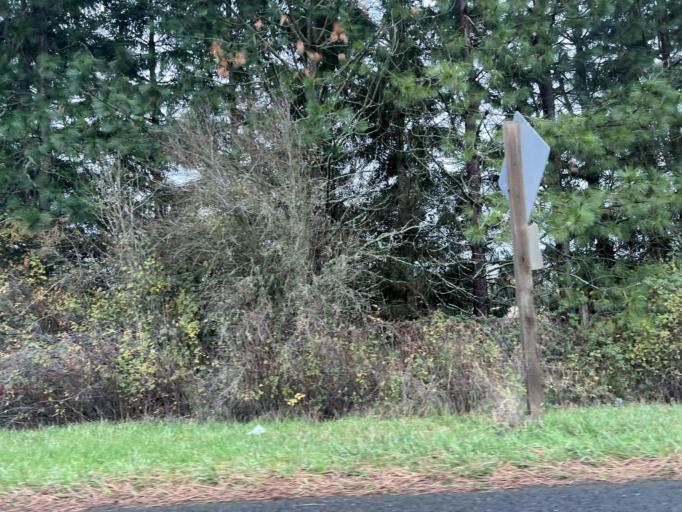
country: US
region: Oregon
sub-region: Polk County
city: Independence
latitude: 44.8088
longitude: -123.0847
